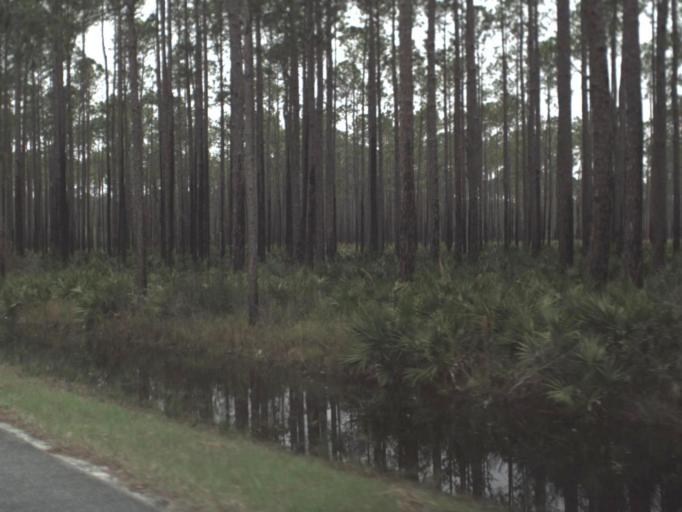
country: US
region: Florida
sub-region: Franklin County
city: Apalachicola
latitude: 29.9310
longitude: -84.9770
